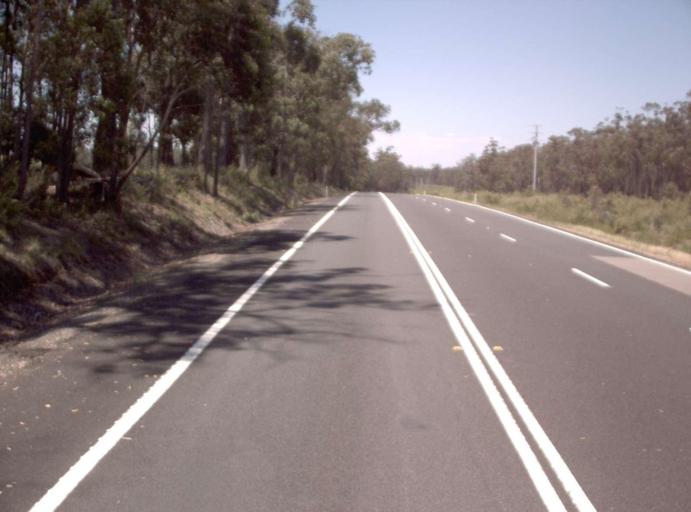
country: AU
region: Victoria
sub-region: East Gippsland
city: Lakes Entrance
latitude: -37.7368
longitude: 148.1494
